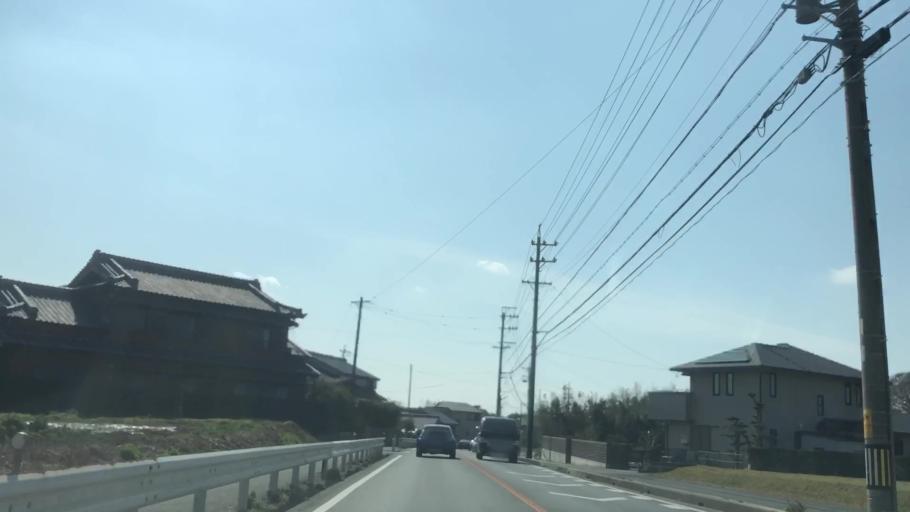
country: JP
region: Aichi
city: Tahara
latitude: 34.6167
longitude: 137.2090
